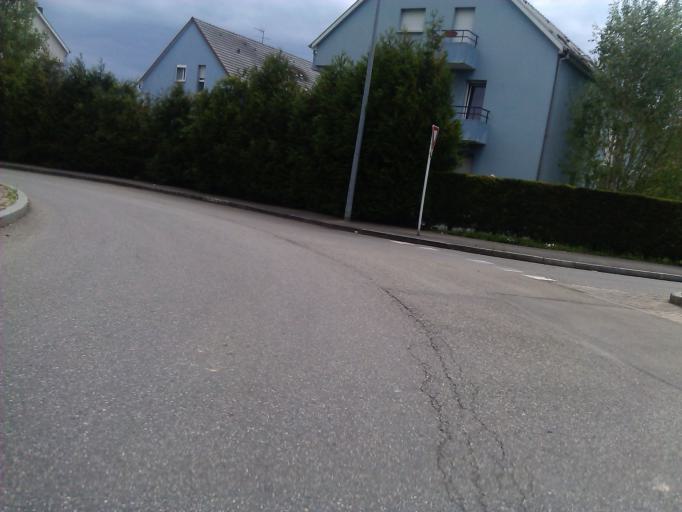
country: FR
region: Alsace
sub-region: Departement du Haut-Rhin
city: Wittenheim
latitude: 47.8141
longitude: 7.3334
